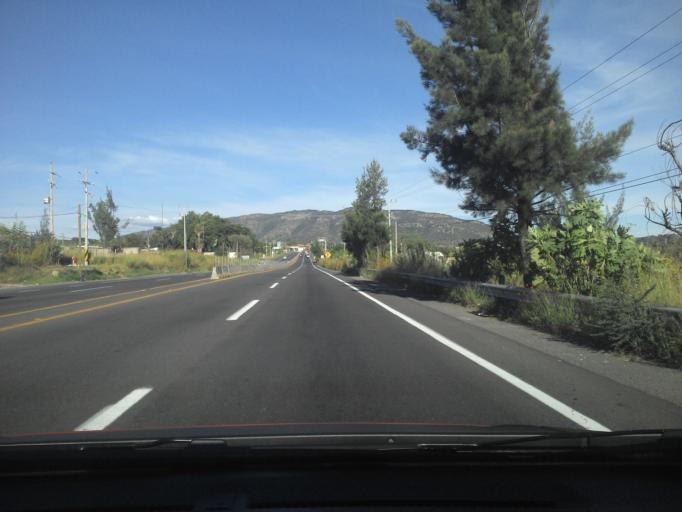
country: MX
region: Jalisco
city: La Venta del Astillero
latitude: 20.7288
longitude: -103.6129
